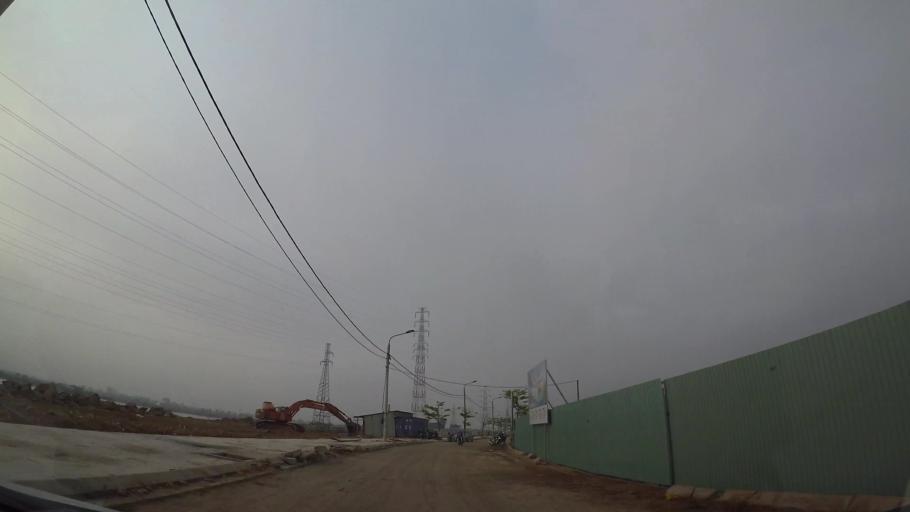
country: VN
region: Da Nang
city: Ngu Hanh Son
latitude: 16.0217
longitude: 108.2378
